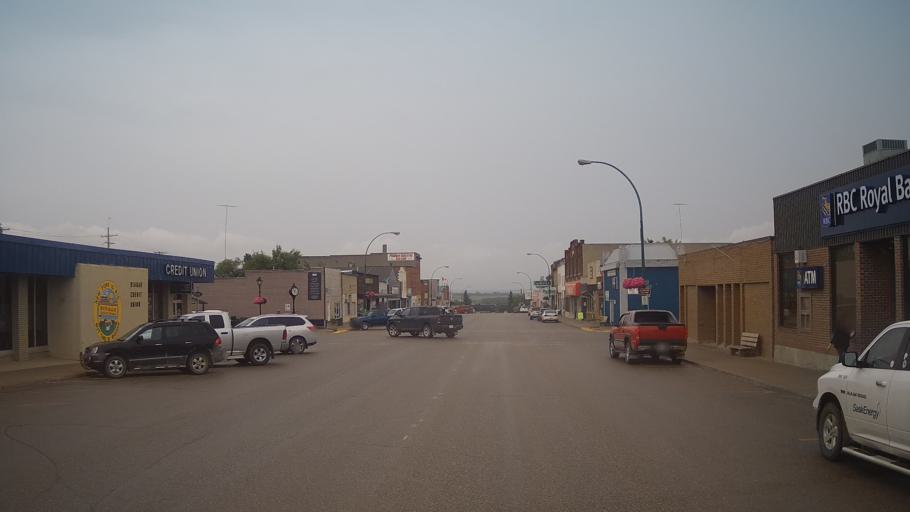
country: CA
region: Saskatchewan
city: Biggar
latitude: 52.0562
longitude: -107.9850
